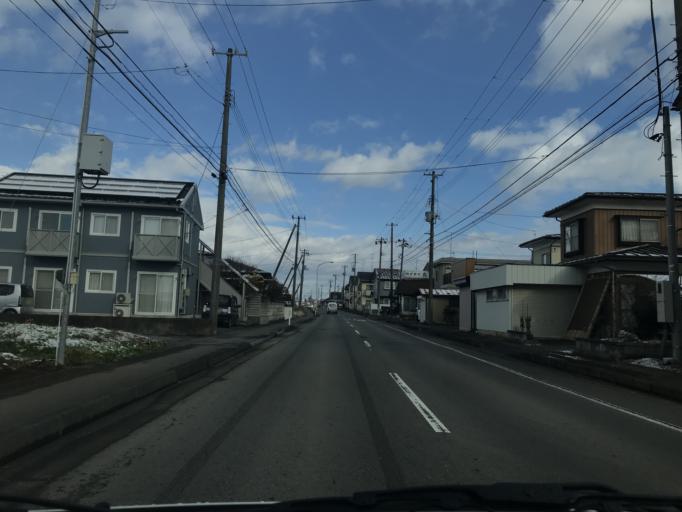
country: JP
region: Iwate
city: Mizusawa
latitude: 39.1114
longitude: 141.1367
